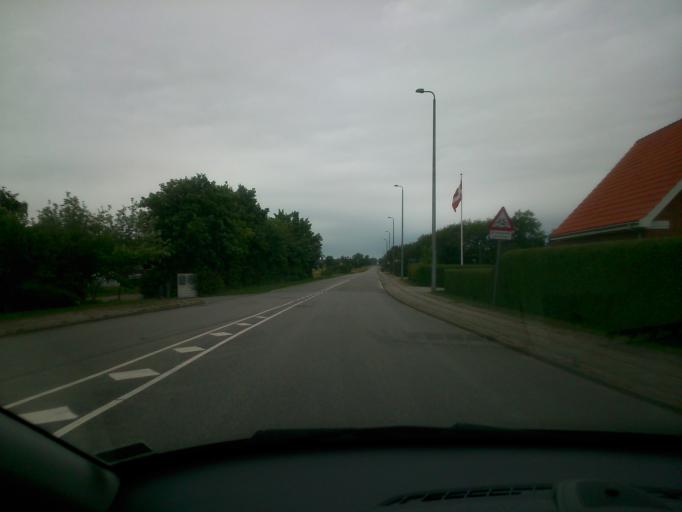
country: DK
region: Central Jutland
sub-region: Ringkobing-Skjern Kommune
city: Skjern
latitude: 55.9554
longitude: 8.4850
